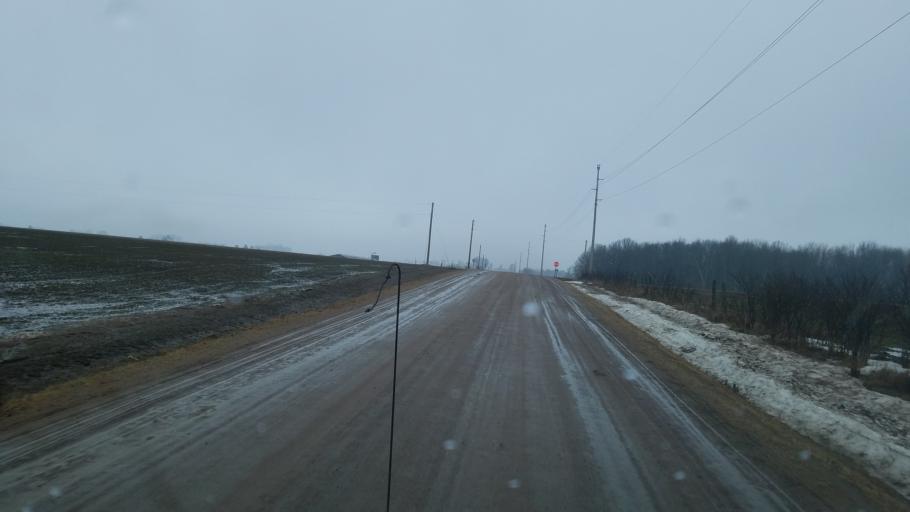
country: US
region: Wisconsin
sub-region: Clark County
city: Loyal
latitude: 44.5985
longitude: -90.3965
